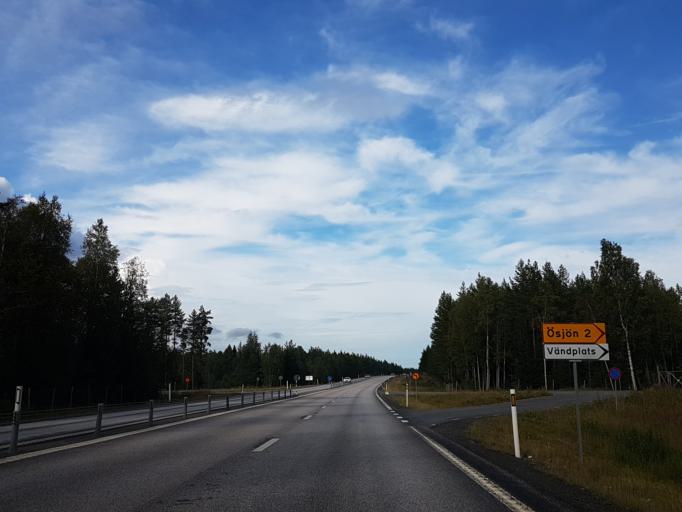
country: SE
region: Vaesterbotten
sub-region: Umea Kommun
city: Saevar
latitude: 63.9811
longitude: 20.7277
